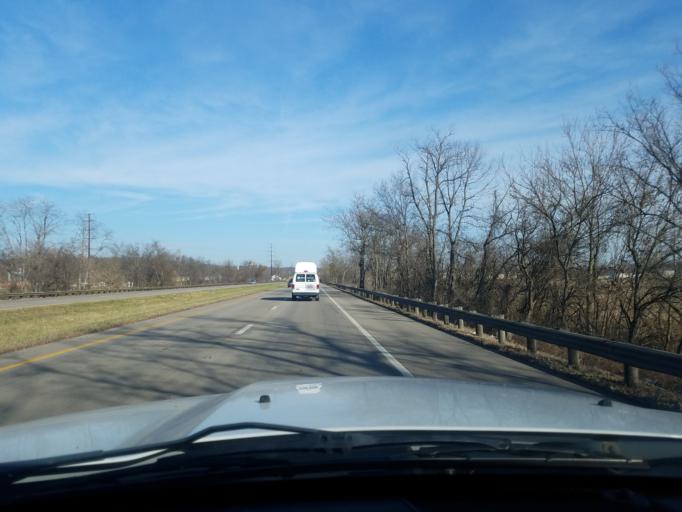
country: US
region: West Virginia
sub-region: Wood County
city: Vienna
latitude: 39.3604
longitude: -81.5432
